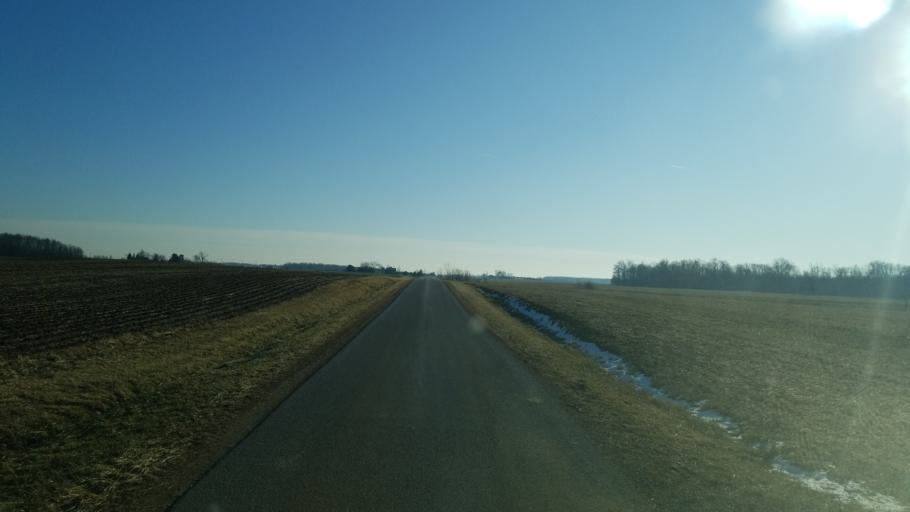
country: US
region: Ohio
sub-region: Sandusky County
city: Green Springs
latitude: 41.1613
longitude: -82.9959
